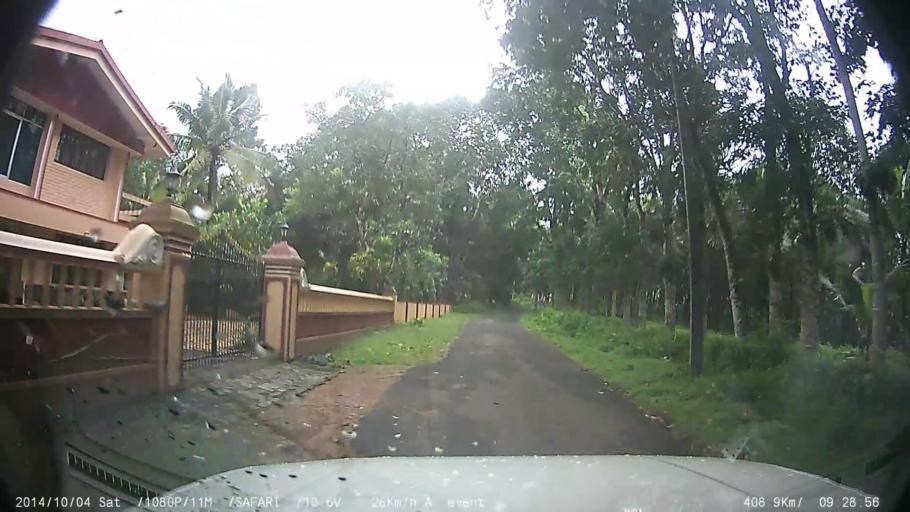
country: IN
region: Kerala
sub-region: Kottayam
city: Palackattumala
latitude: 9.7873
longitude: 76.5730
